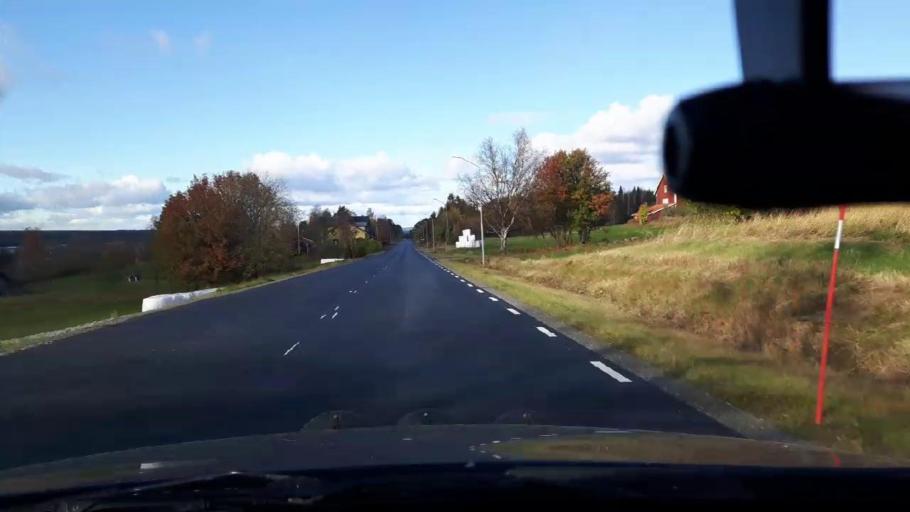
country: SE
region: Jaemtland
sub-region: Bergs Kommun
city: Hoverberg
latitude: 62.9676
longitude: 14.4886
